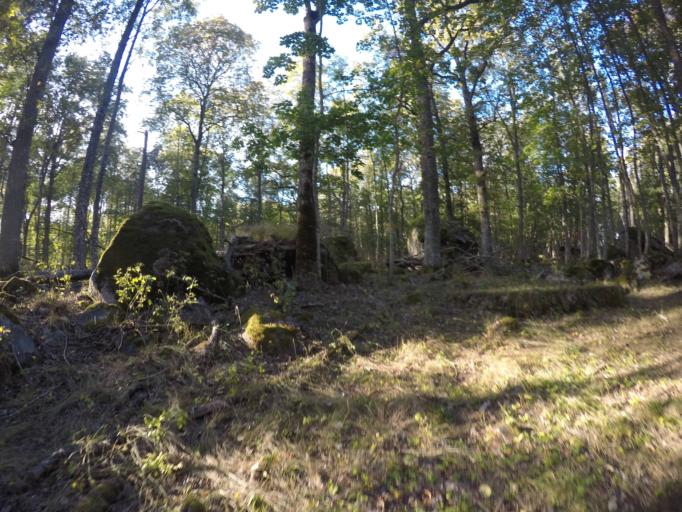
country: SE
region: Soedermanland
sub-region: Eskilstuna Kommun
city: Kvicksund
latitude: 59.4780
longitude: 16.2419
